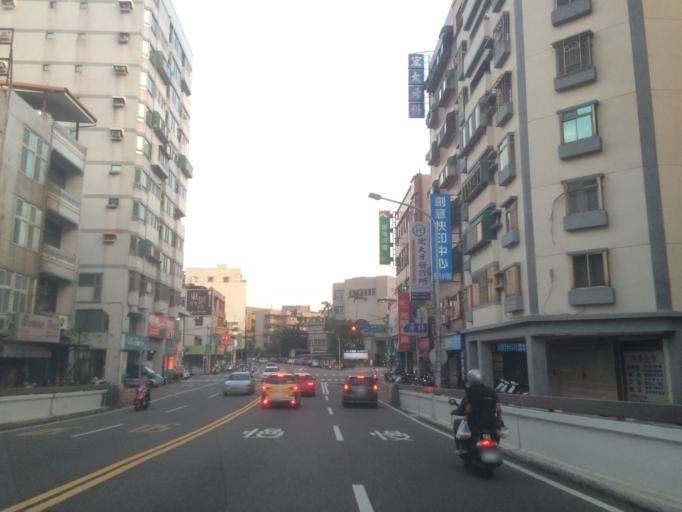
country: TW
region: Taiwan
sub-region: Hsinchu
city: Hsinchu
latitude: 24.7954
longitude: 120.9648
